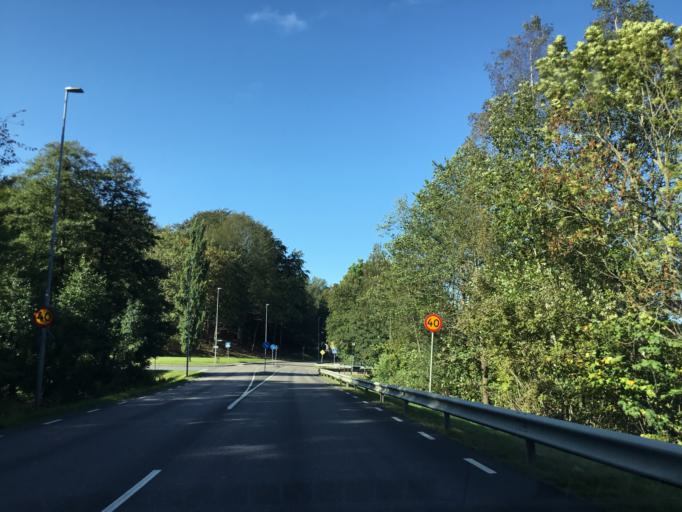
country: SE
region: Vaestra Goetaland
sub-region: Molndal
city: Moelndal
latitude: 57.6542
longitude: 12.0472
